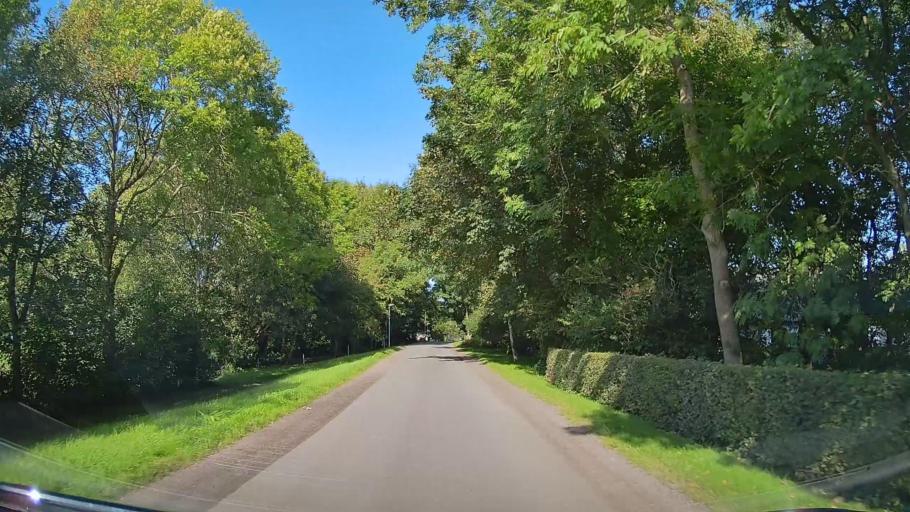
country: DE
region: Lower Saxony
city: Padingbuttel
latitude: 53.7264
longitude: 8.5300
